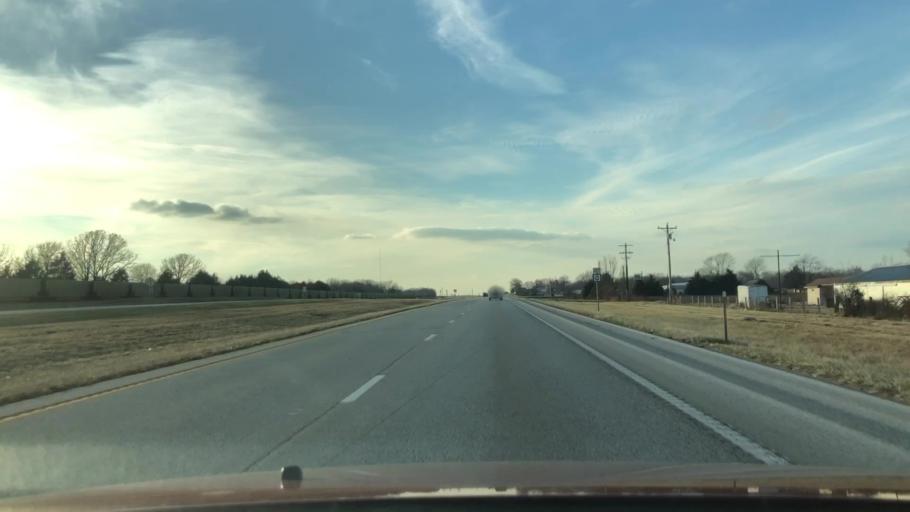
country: US
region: Missouri
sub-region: Webster County
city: Seymour
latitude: 37.1716
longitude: -92.8427
